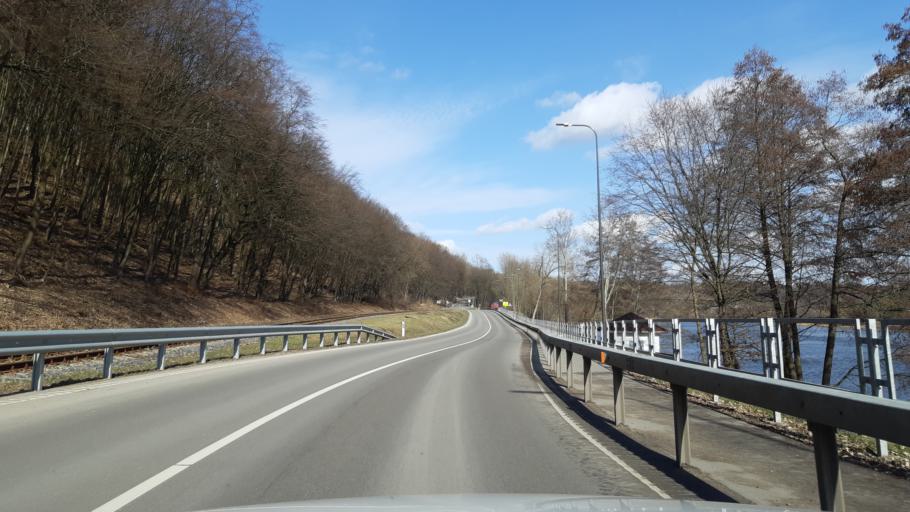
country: LT
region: Kauno apskritis
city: Dainava (Kaunas)
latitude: 54.8848
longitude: 23.9560
